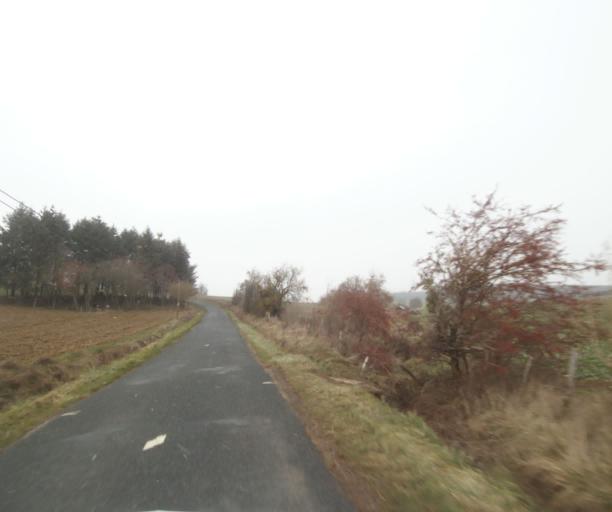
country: FR
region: Champagne-Ardenne
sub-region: Departement de la Haute-Marne
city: Wassy
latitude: 48.5116
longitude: 5.0141
